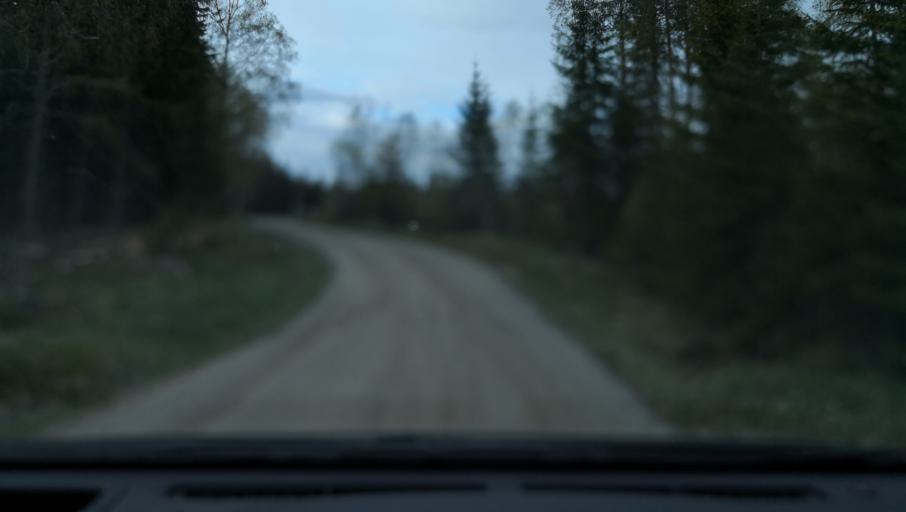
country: SE
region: Dalarna
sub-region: Saters Kommun
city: Saeter
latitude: 60.2070
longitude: 15.7449
